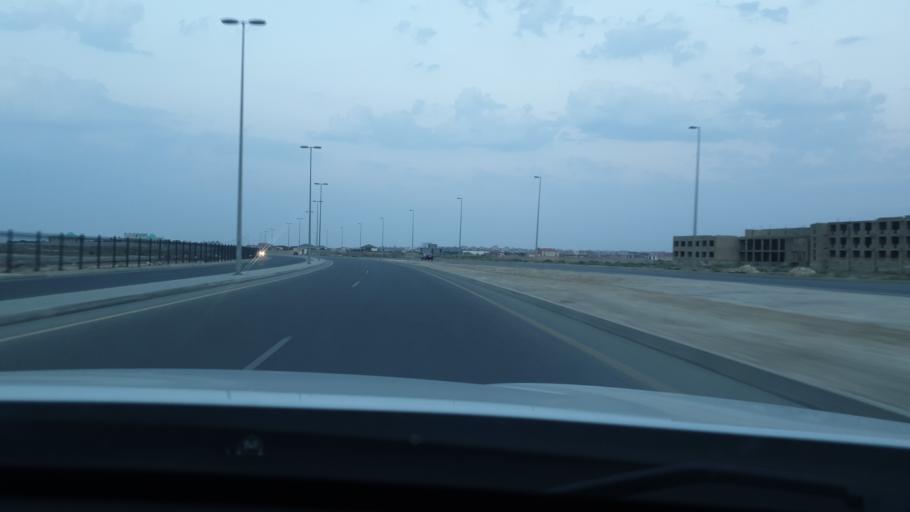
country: AZ
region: Baki
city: Nardaran
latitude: 40.5822
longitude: 50.0053
